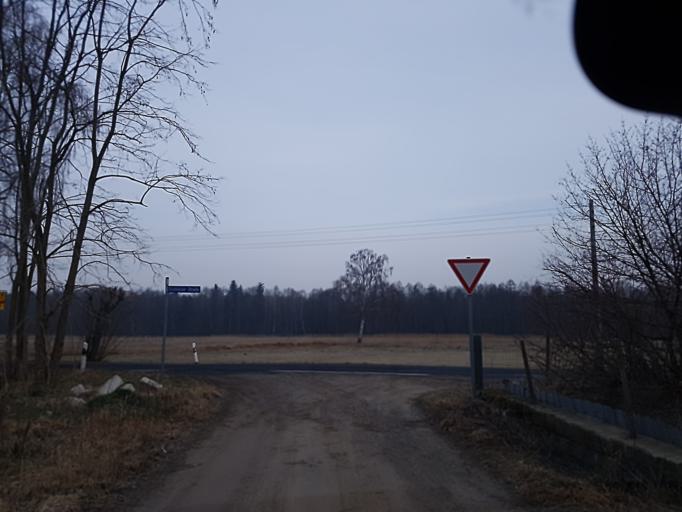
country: DE
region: Brandenburg
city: Finsterwalde
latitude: 51.6222
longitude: 13.6909
